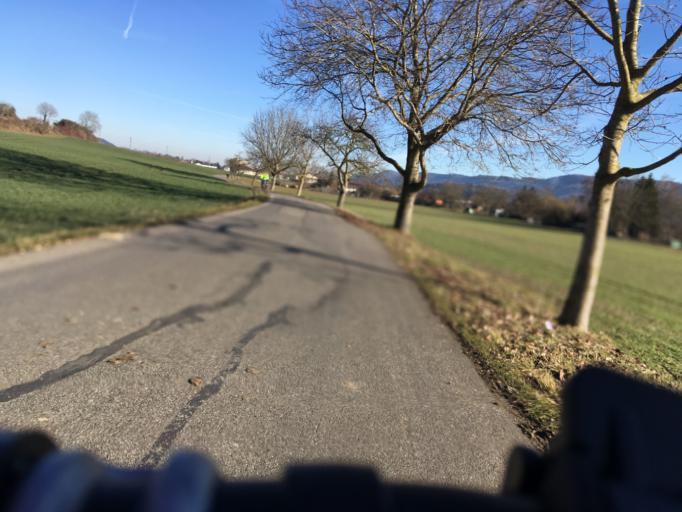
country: CH
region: Schaffhausen
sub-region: Bezirk Stein
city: Ramsen
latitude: 47.7303
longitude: 8.8130
